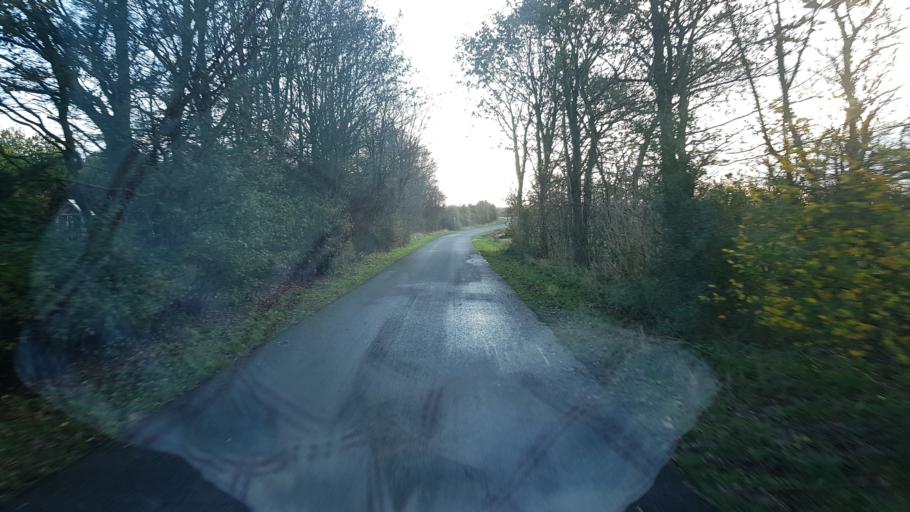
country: DK
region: South Denmark
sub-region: Vejen Kommune
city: Holsted
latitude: 55.4670
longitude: 8.9475
